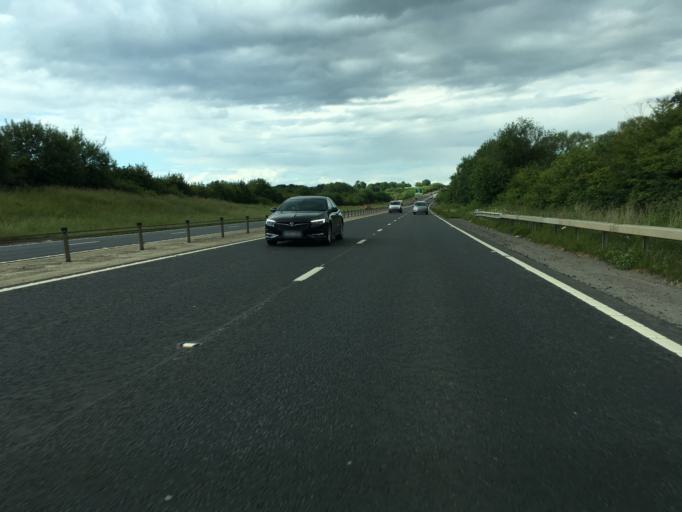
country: GB
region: England
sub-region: Central Bedfordshire
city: Leighton Buzzard
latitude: 51.9197
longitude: -0.6997
